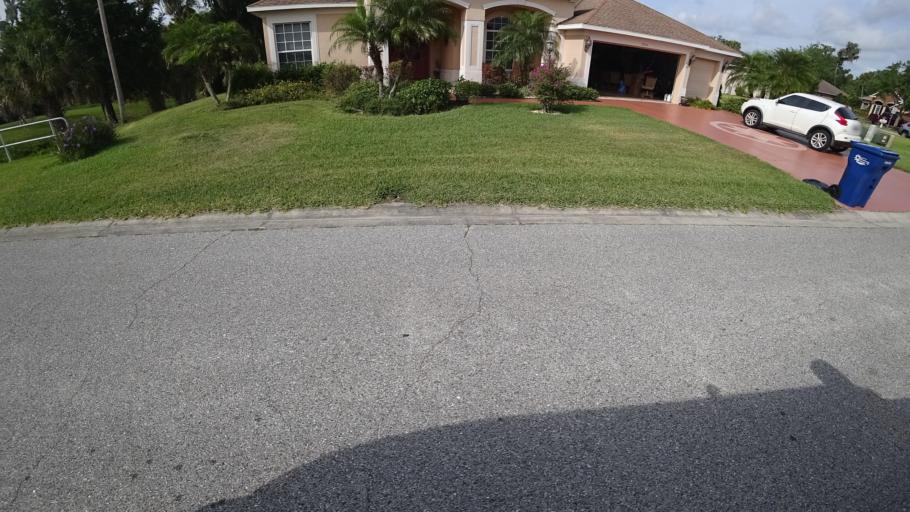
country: US
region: Florida
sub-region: Manatee County
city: Ellenton
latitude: 27.5634
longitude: -82.4701
